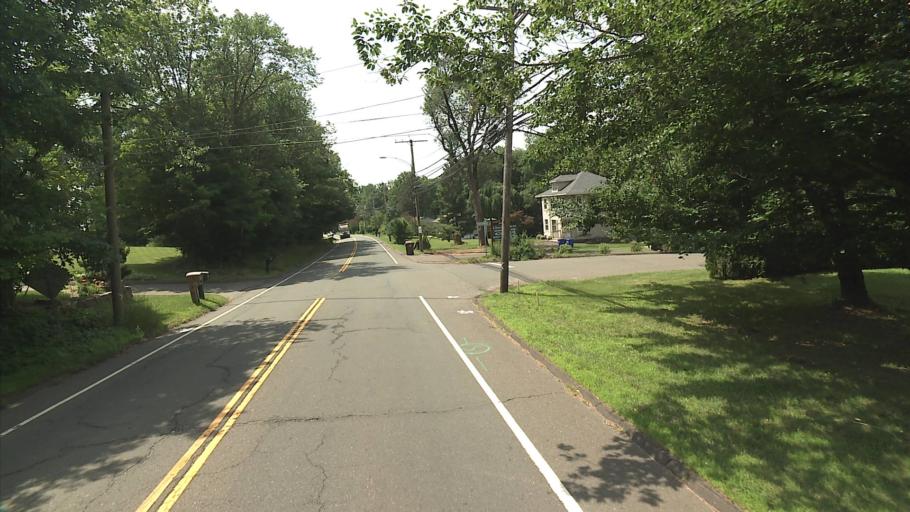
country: US
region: Connecticut
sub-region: New Haven County
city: North Branford
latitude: 41.3117
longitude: -72.7713
